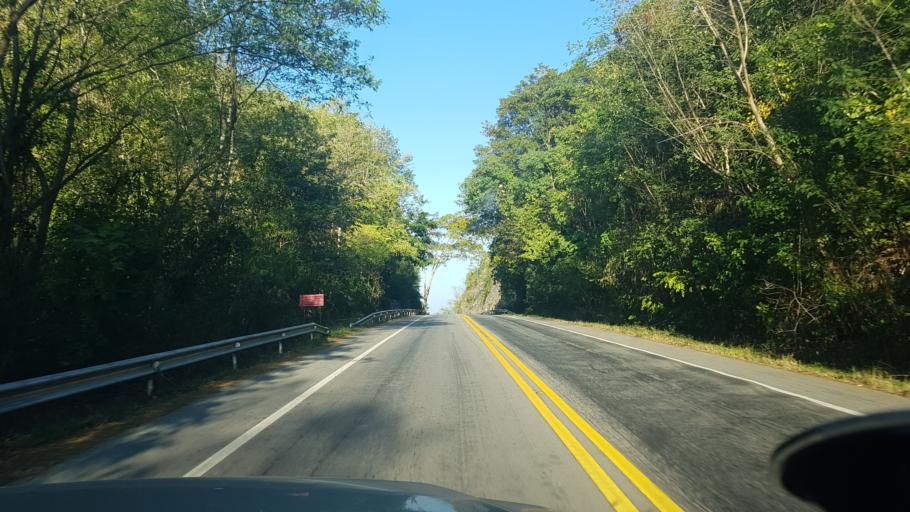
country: TH
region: Khon Kaen
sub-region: Amphoe Phu Pha Man
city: Phu Pha Man
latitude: 16.6460
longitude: 101.7897
